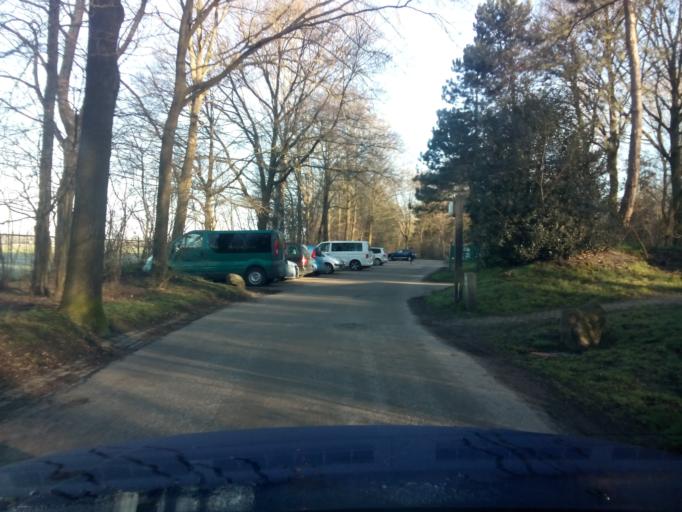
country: NL
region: Drenthe
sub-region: Gemeente Coevorden
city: Coevorden
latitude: 52.6734
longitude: 6.7637
